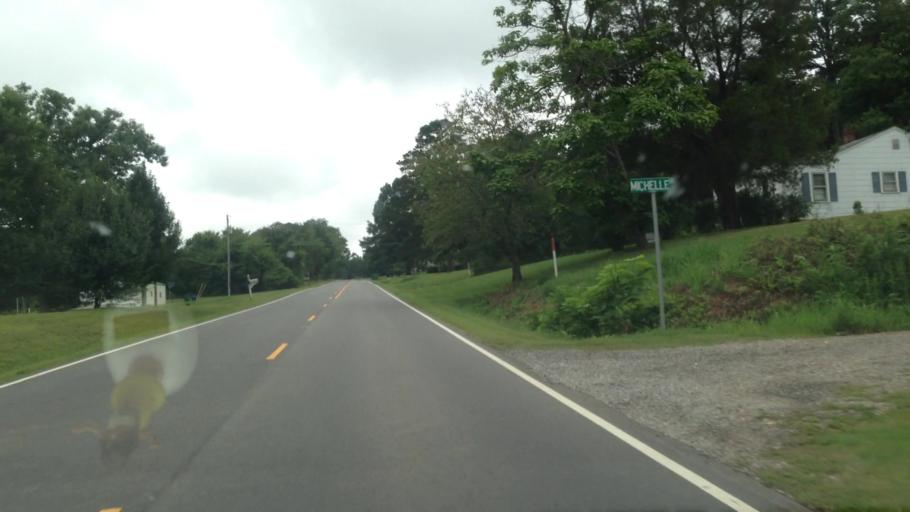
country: US
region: North Carolina
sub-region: Rockingham County
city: Mayodan
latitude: 36.4096
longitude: -79.9966
